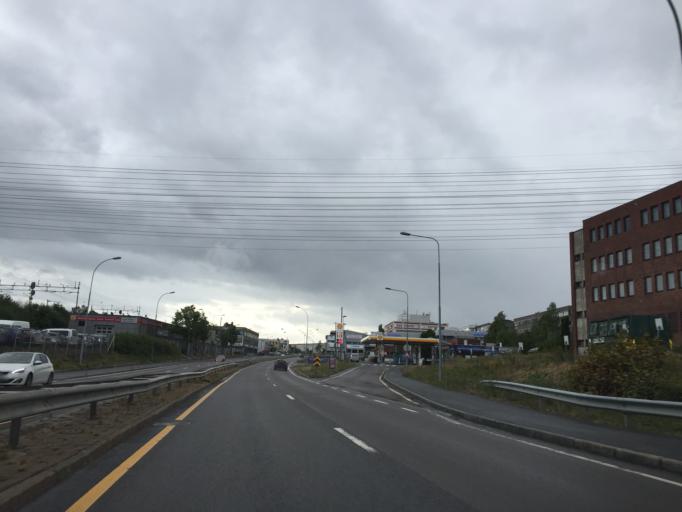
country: NO
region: Akershus
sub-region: Lorenskog
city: Kjenn
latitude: 59.9480
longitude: 10.8811
